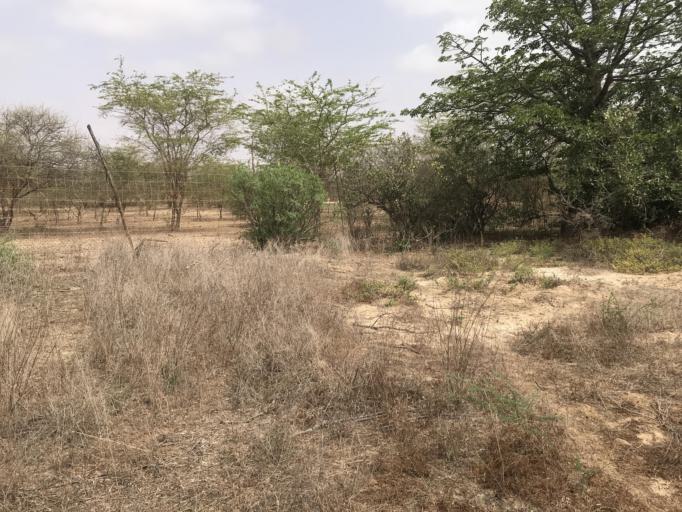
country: SN
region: Saint-Louis
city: Saint-Louis
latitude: 15.9199
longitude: -16.4528
